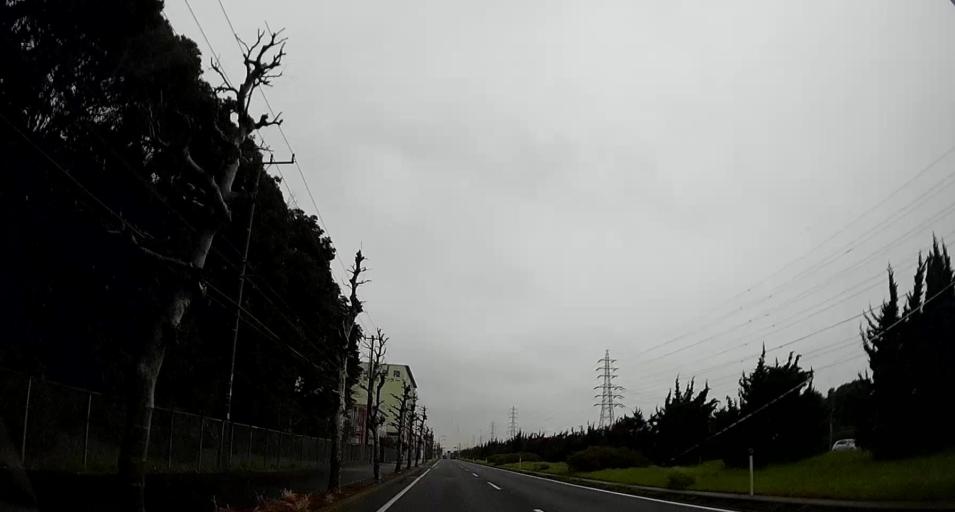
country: JP
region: Chiba
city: Ichihara
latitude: 35.5098
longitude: 140.0552
